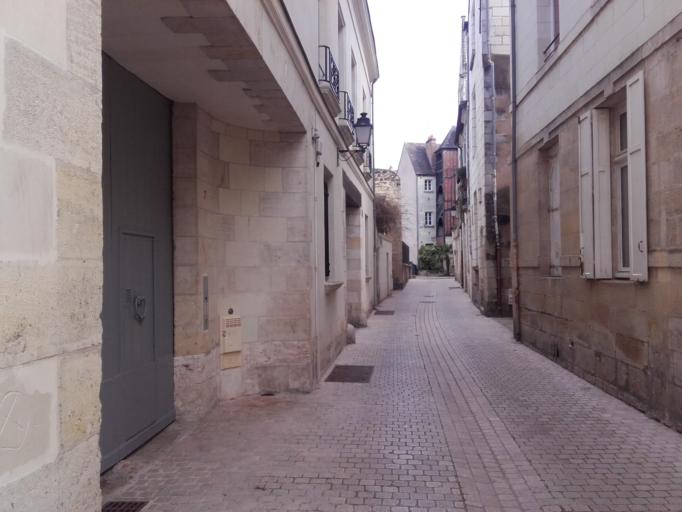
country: FR
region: Centre
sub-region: Departement d'Indre-et-Loire
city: La Riche
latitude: 47.3951
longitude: 0.6807
